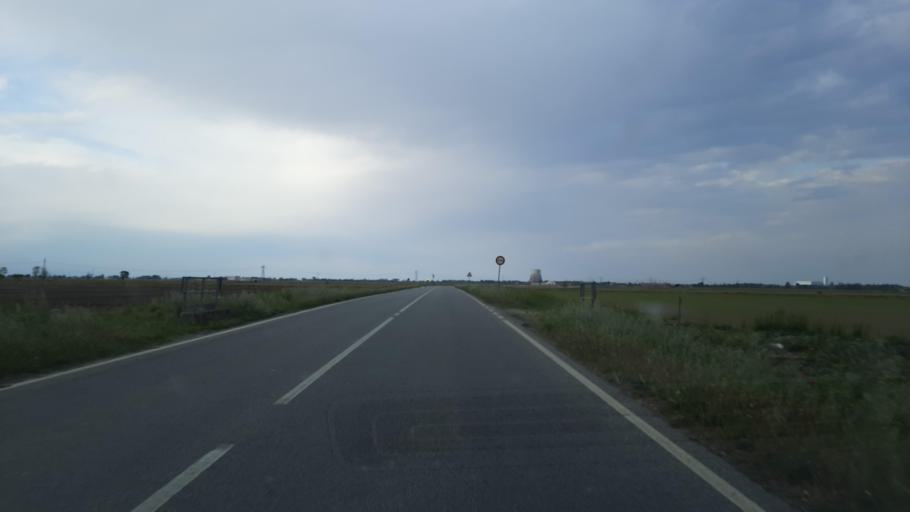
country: IT
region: Piedmont
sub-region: Provincia di Vercelli
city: Lamporo
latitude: 45.2253
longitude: 8.1473
